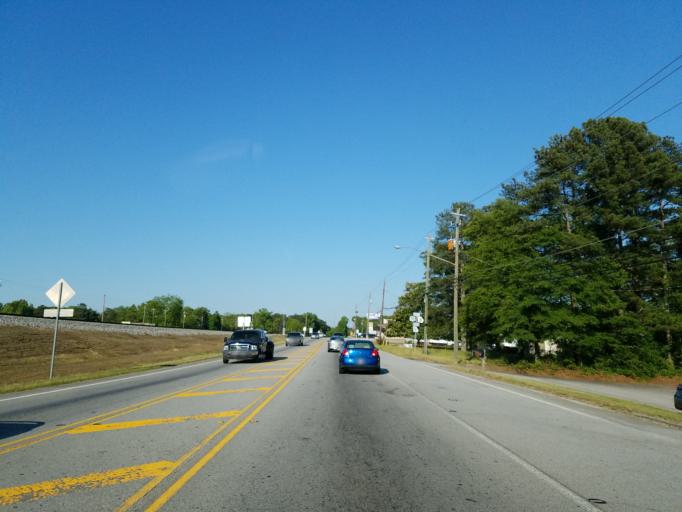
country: US
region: Georgia
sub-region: Douglas County
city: Douglasville
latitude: 33.7430
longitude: -84.7754
